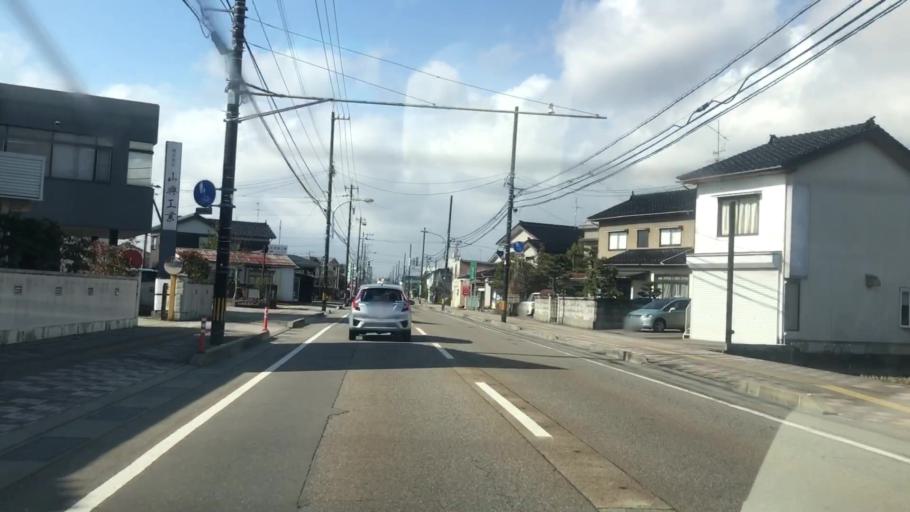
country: JP
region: Toyama
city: Takaoka
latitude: 36.7287
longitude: 137.0587
